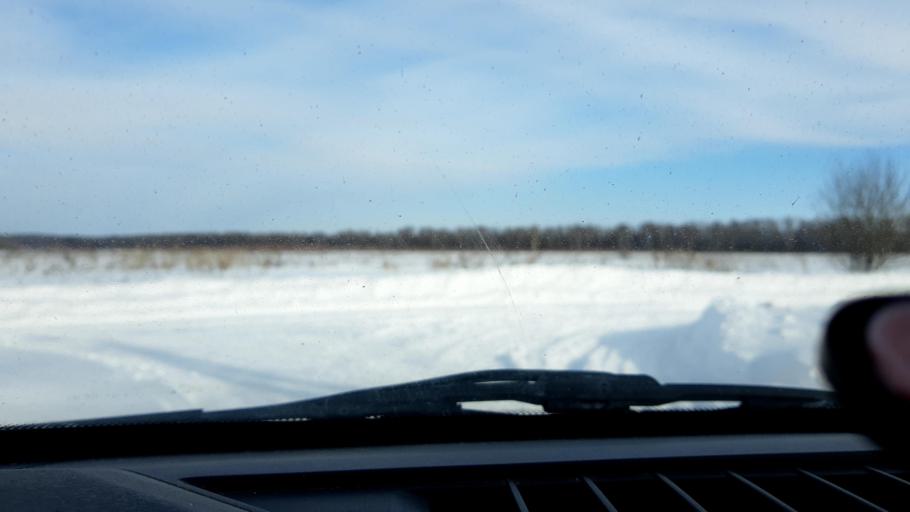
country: RU
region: Bashkortostan
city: Iglino
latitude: 54.7889
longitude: 56.2803
